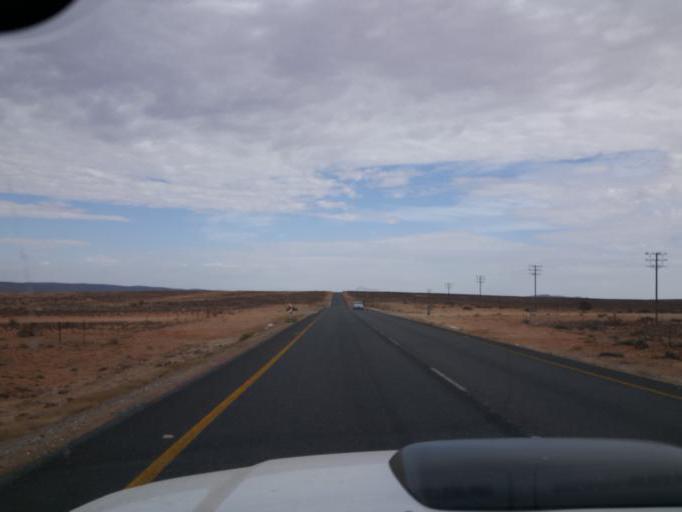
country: ZA
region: Northern Cape
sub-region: Namakwa District Municipality
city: Springbok
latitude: -29.3462
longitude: 17.7813
